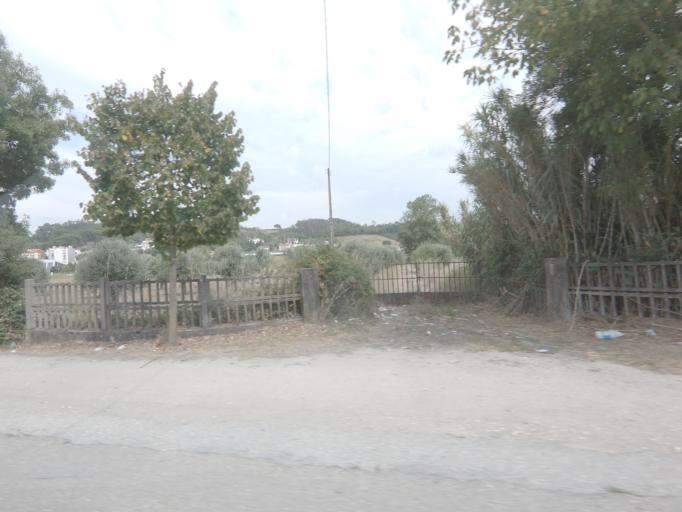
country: PT
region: Leiria
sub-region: Pombal
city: Pombal
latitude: 39.9074
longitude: -8.6331
